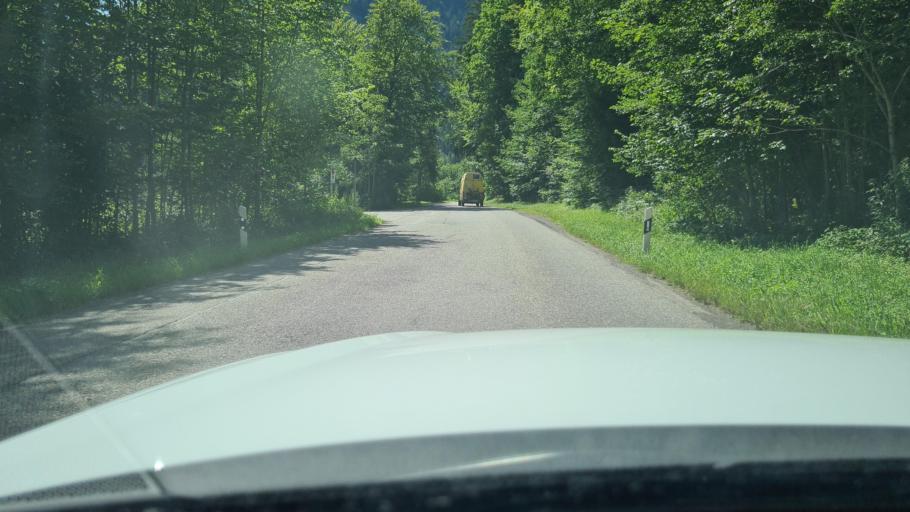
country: DE
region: Bavaria
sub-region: Swabia
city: Oberstdorf
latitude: 47.3844
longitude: 10.2812
